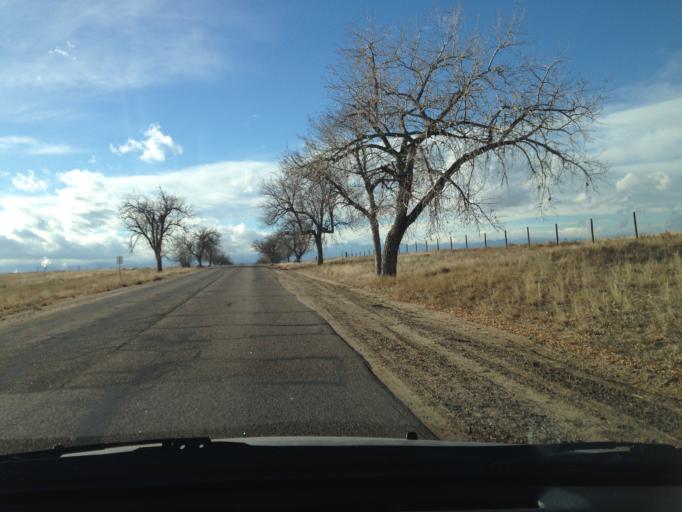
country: US
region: Colorado
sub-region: Adams County
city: Derby
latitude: 39.8273
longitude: -104.8812
